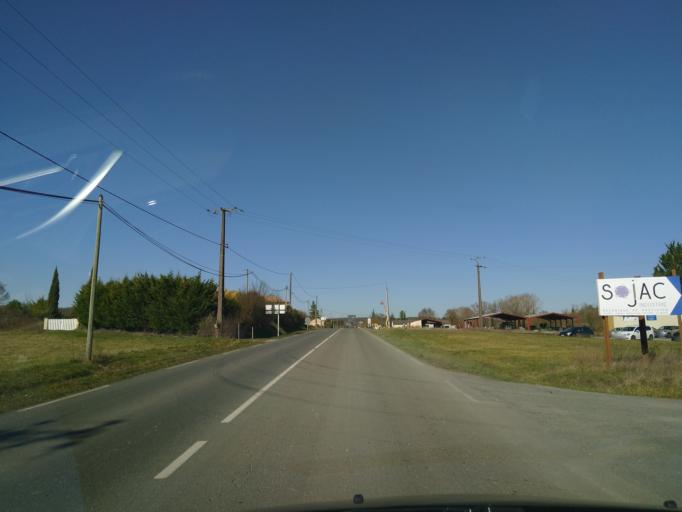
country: FR
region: Aquitaine
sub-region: Departement du Lot-et-Garonne
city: Castillonnes
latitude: 44.7055
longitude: 0.5625
